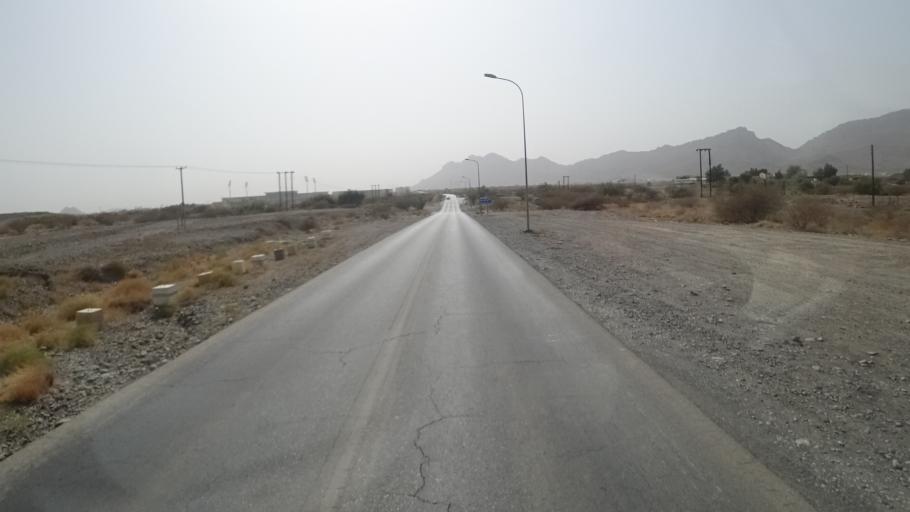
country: OM
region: Muhafazat ad Dakhiliyah
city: Nizwa
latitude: 22.9120
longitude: 57.5991
